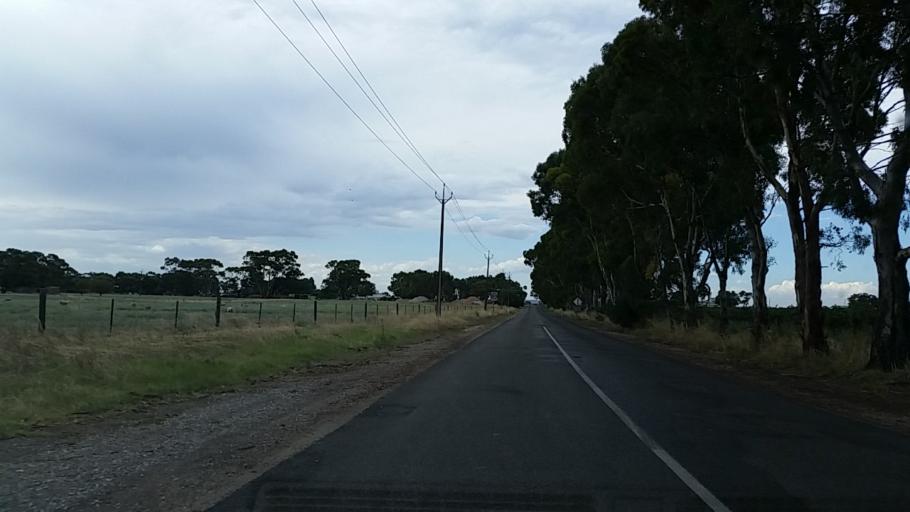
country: AU
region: South Australia
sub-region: Barossa
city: Nuriootpa
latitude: -34.4950
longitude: 139.0131
